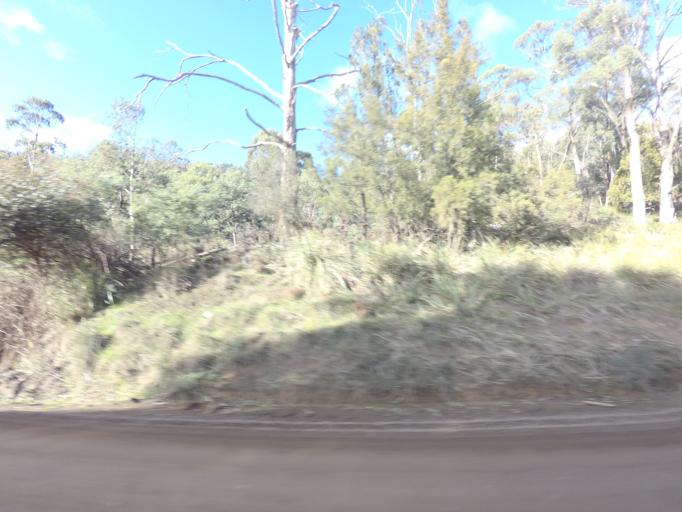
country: AU
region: Tasmania
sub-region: Derwent Valley
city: New Norfolk
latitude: -42.8152
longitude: 147.1297
